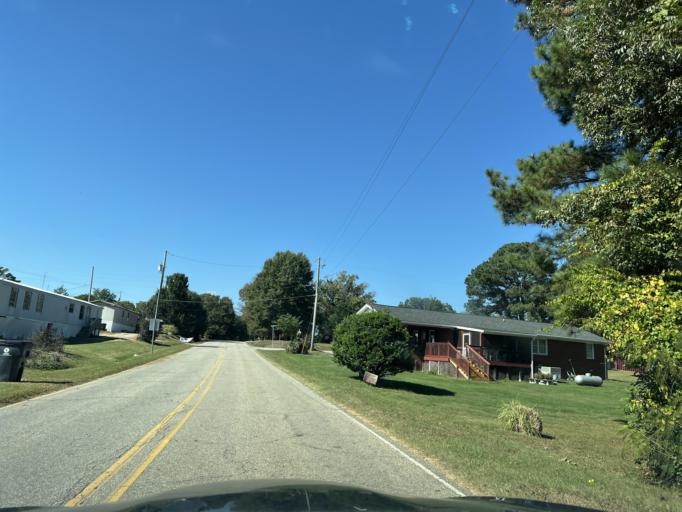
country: US
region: North Carolina
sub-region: Johnston County
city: Clayton
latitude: 35.6658
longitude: -78.4725
